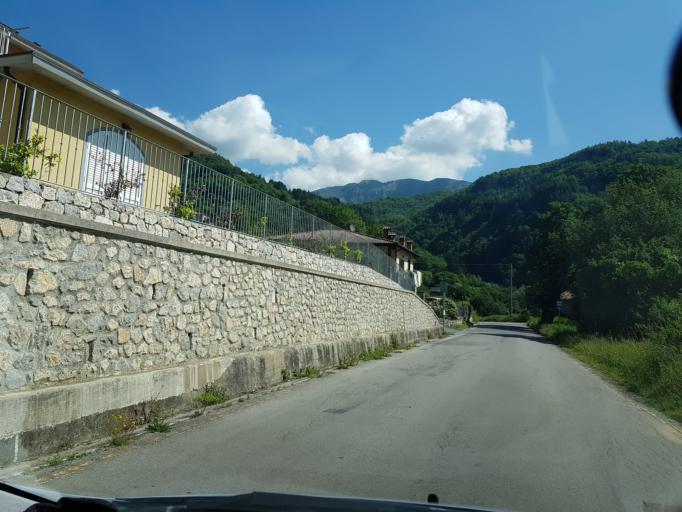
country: IT
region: Tuscany
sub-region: Provincia di Lucca
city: San Romano in Garfagnana
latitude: 44.1651
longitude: 10.3461
